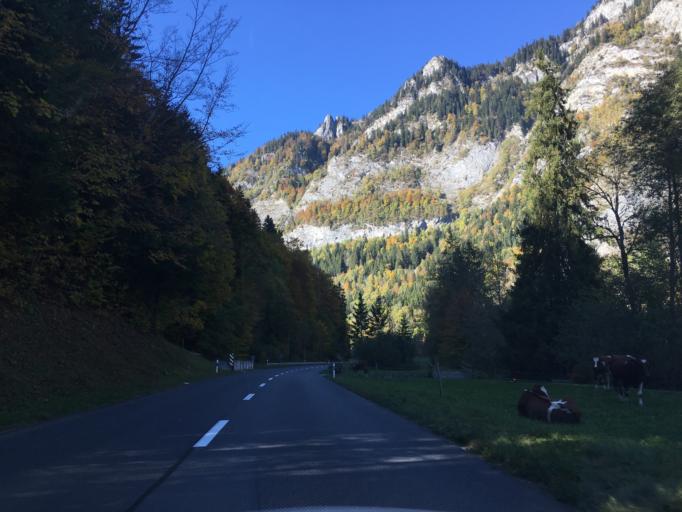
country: CH
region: Fribourg
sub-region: Gruyere District
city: Charmey
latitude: 46.6040
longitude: 7.2001
